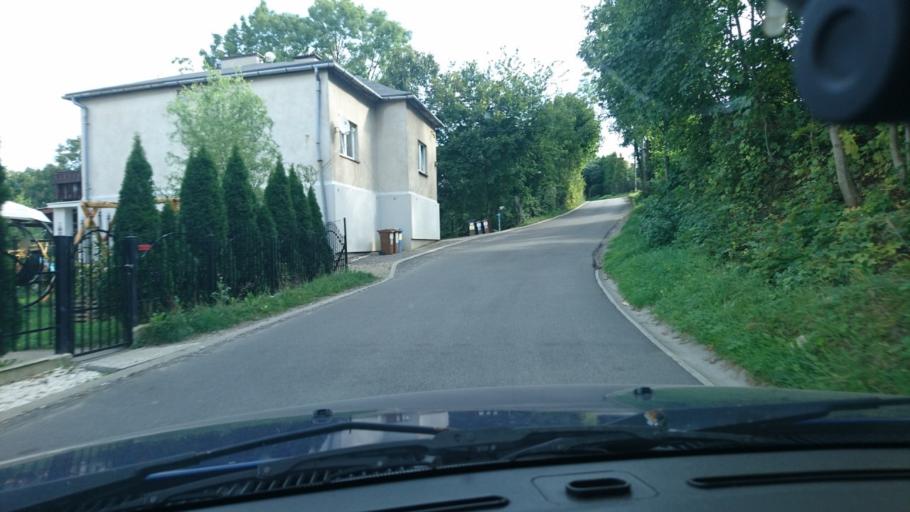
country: PL
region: Silesian Voivodeship
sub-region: Powiat bielski
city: Mazancowice
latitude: 49.8187
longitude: 18.9915
